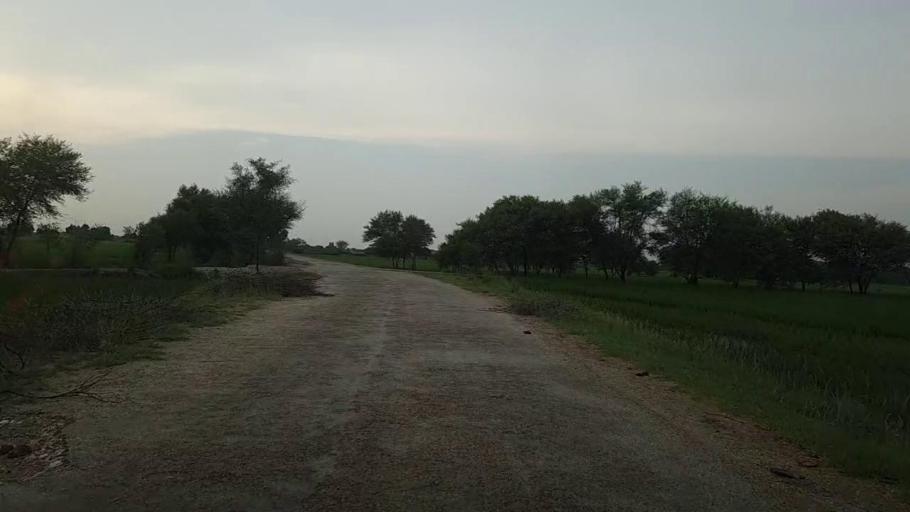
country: PK
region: Sindh
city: Khanpur
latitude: 27.8426
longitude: 69.4646
